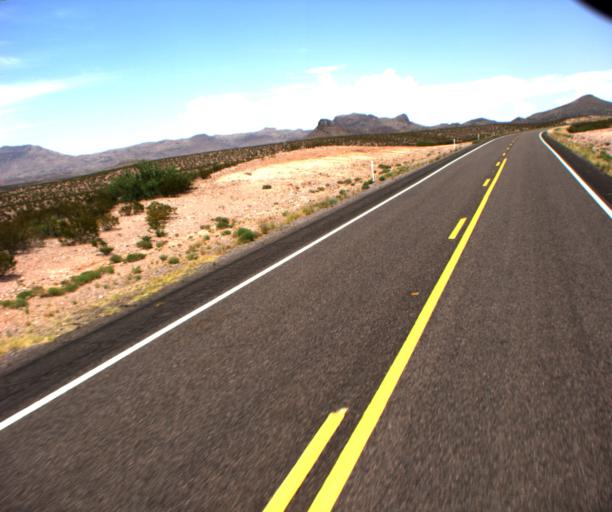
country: US
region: Arizona
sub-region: Greenlee County
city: Clifton
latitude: 32.7527
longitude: -109.3752
